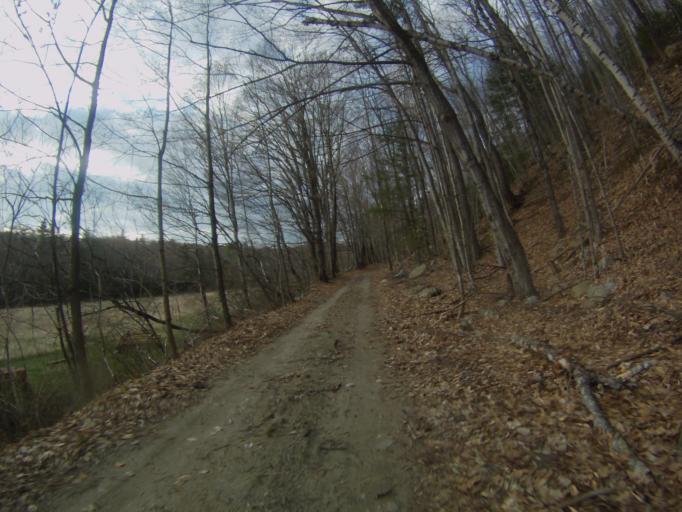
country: US
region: Vermont
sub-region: Rutland County
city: Brandon
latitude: 43.8391
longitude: -73.0409
